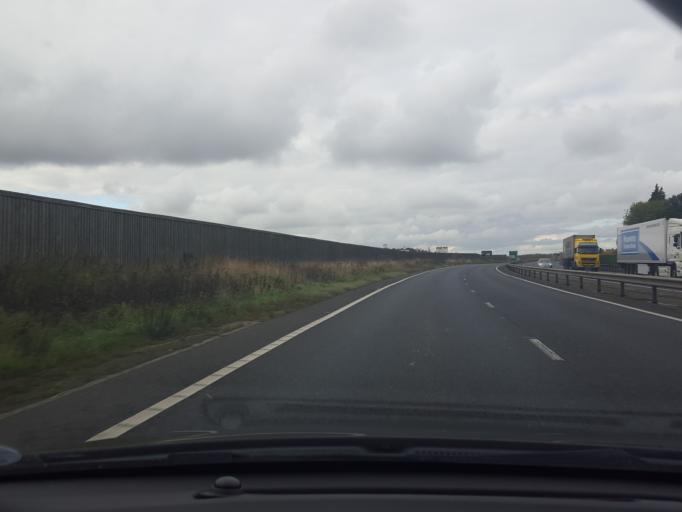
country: GB
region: England
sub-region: Suffolk
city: Stowmarket
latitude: 52.1994
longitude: 0.9861
